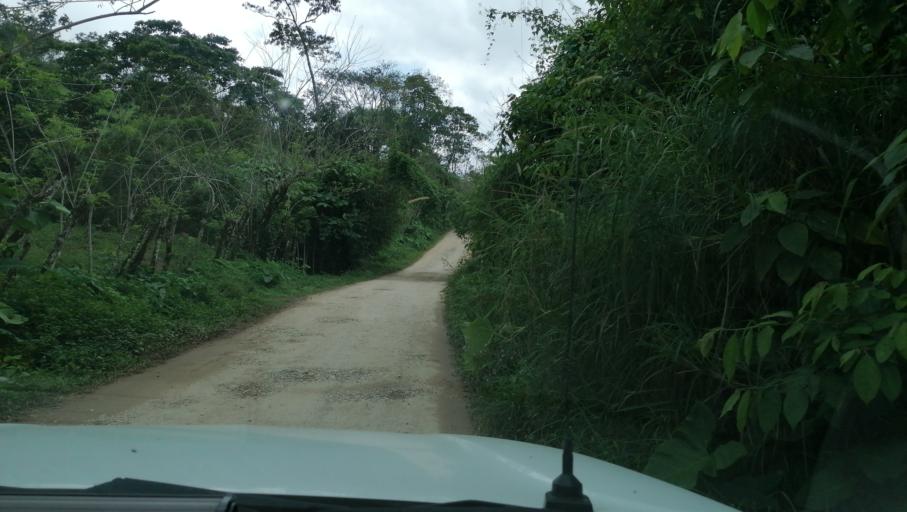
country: MX
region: Chiapas
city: Ocotepec
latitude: 17.2775
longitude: -93.2295
